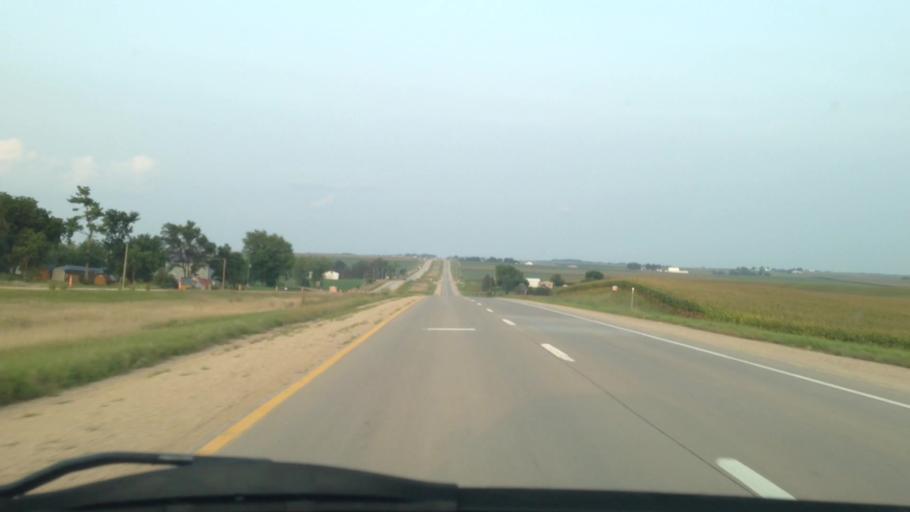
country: US
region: Iowa
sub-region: Benton County
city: Atkins
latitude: 41.9633
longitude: -91.9992
